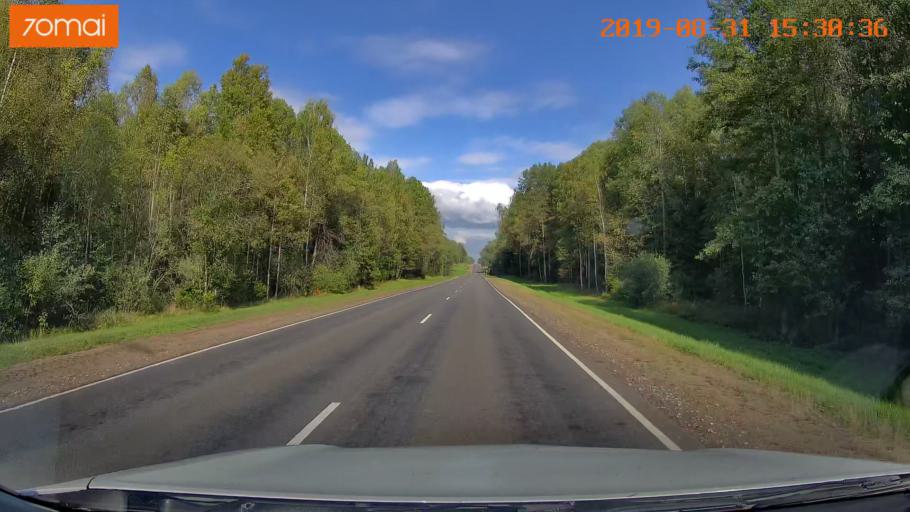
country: RU
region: Kaluga
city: Baryatino
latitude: 54.5768
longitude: 34.6341
